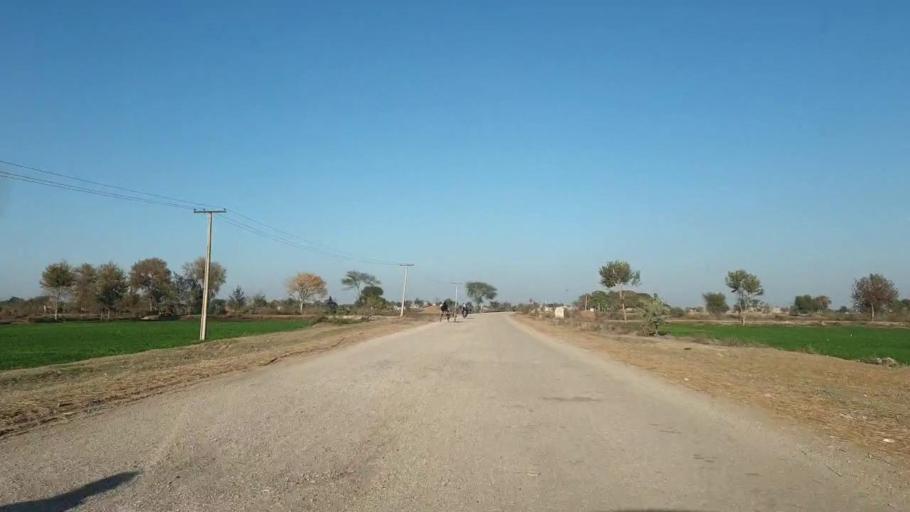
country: PK
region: Sindh
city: Dokri
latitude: 27.3705
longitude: 68.1186
